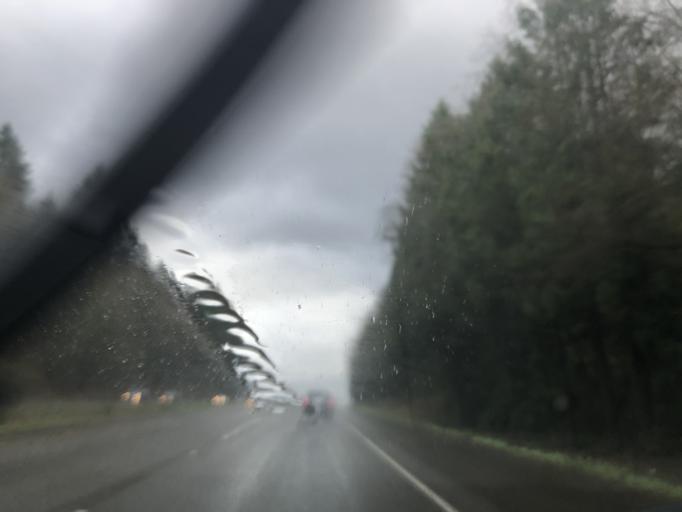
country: US
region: Washington
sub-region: Pierce County
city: Gig Harbor
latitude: 47.3273
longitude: -122.5963
